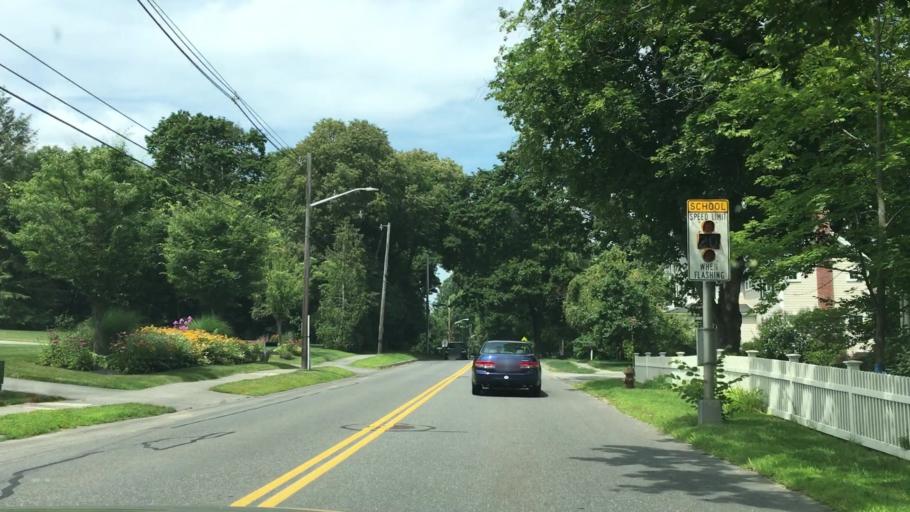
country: US
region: Massachusetts
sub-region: Middlesex County
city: Concord
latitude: 42.4521
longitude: -71.3487
